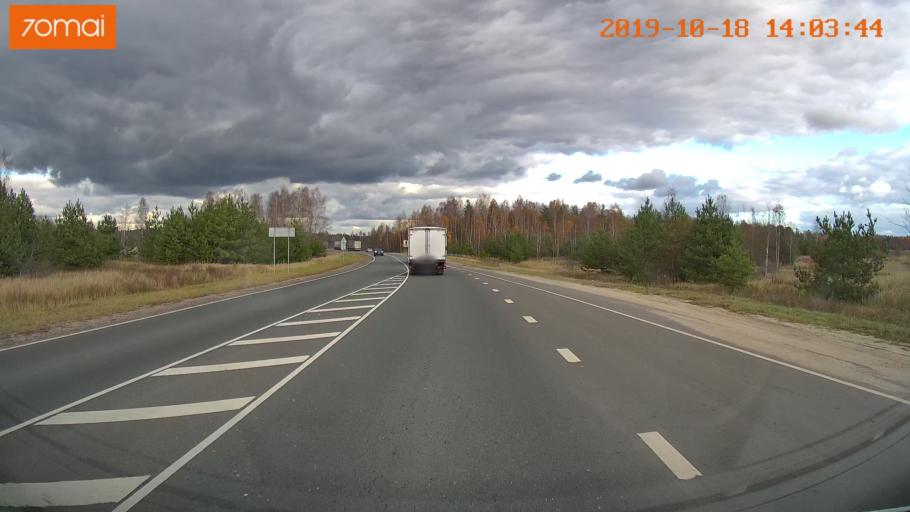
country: RU
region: Rjazan
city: Spas-Klepiki
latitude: 55.1188
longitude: 40.1307
